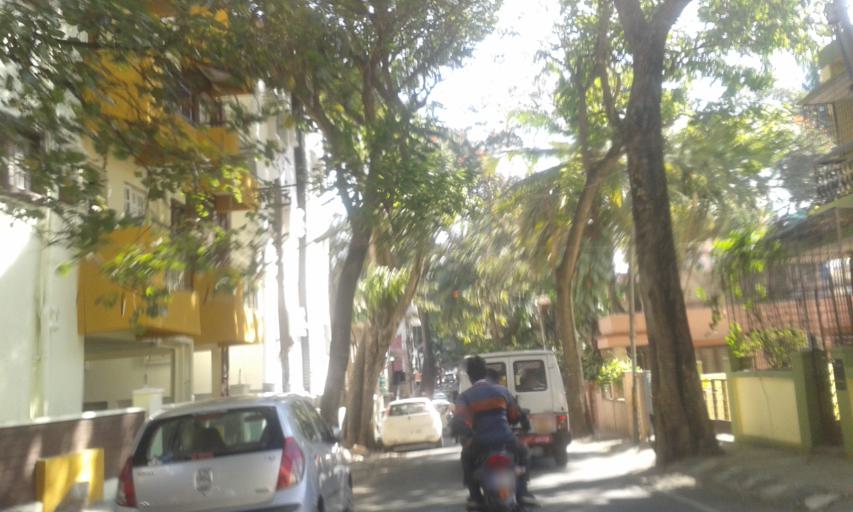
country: IN
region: Karnataka
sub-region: Bangalore Urban
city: Bangalore
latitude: 12.9303
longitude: 77.5870
